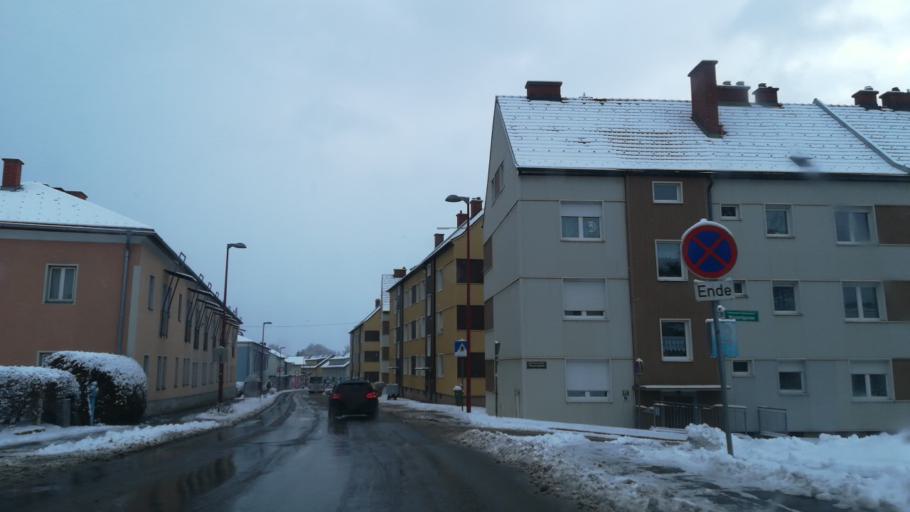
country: AT
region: Styria
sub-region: Politischer Bezirk Murtal
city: Fohnsdorf
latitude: 47.2056
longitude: 14.6660
